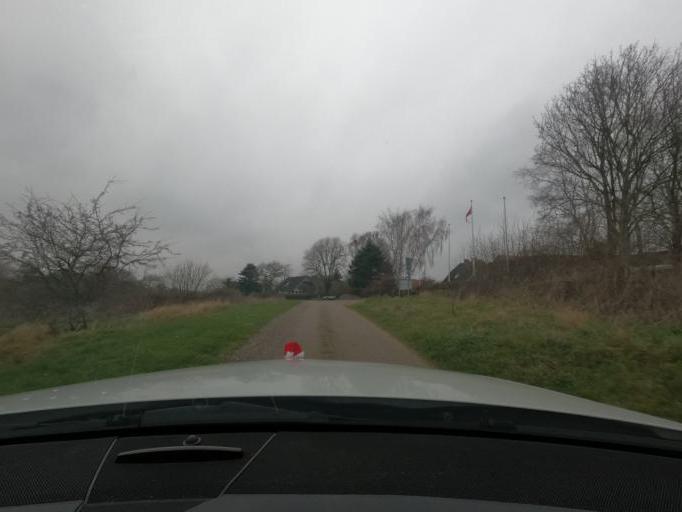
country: DK
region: South Denmark
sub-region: Haderslev Kommune
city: Starup
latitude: 55.1856
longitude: 9.6545
